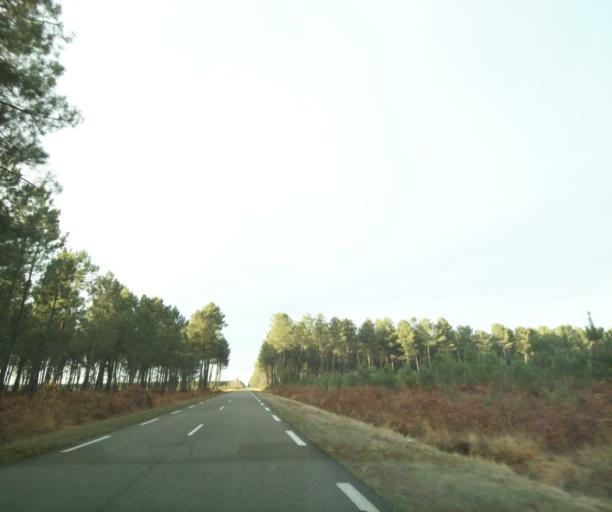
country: FR
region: Aquitaine
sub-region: Departement des Landes
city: Gabarret
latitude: 44.1295
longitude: -0.1131
